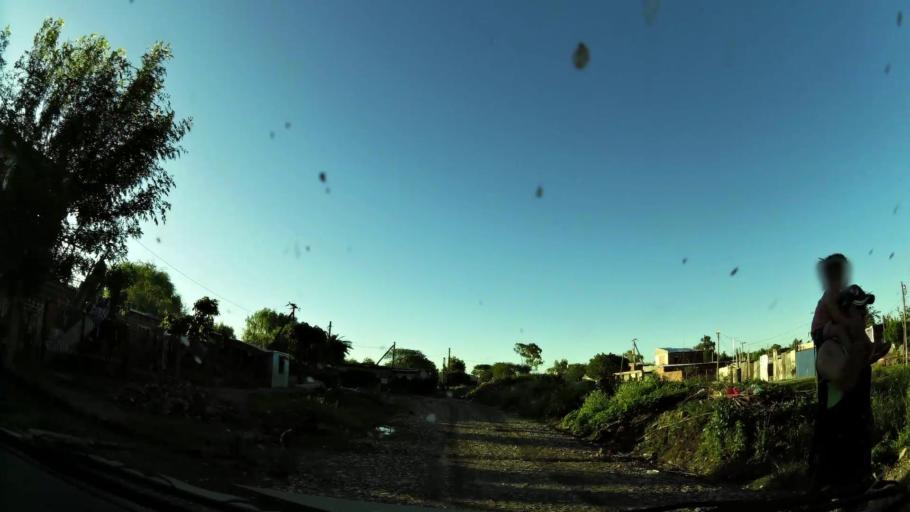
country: AR
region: Buenos Aires
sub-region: Partido de Almirante Brown
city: Adrogue
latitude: -34.7723
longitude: -58.3308
